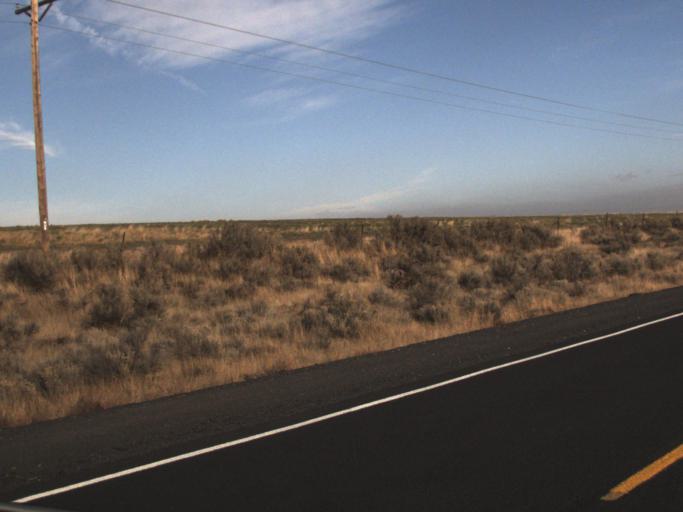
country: US
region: Washington
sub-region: Grant County
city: Warden
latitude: 47.3339
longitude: -118.8892
